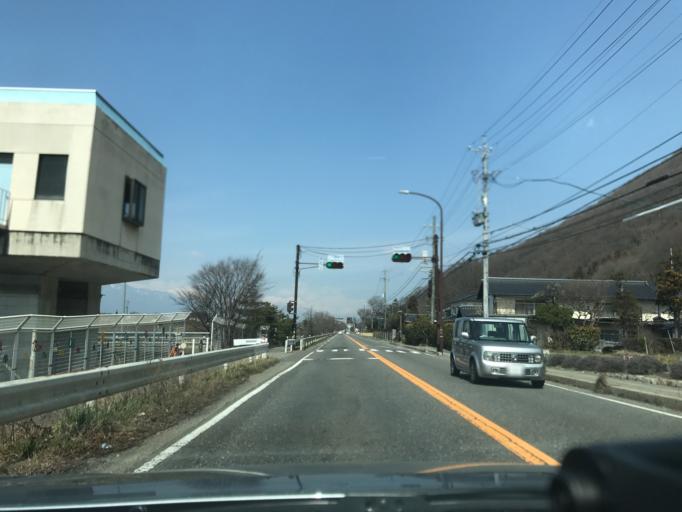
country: JP
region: Nagano
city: Matsumoto
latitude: 36.2539
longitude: 137.9509
